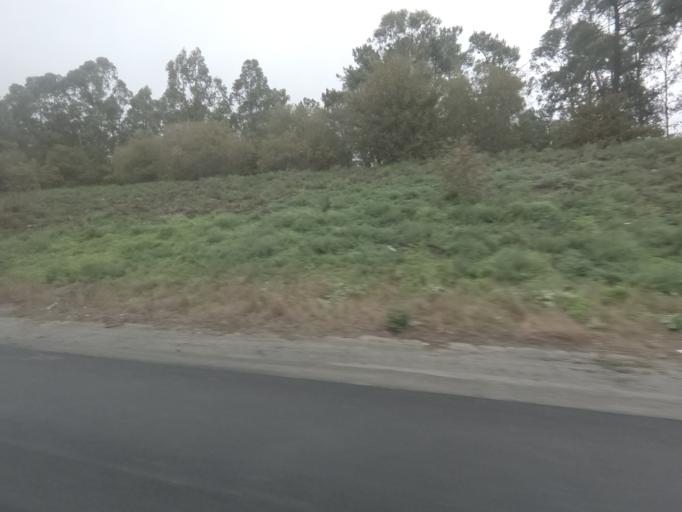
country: ES
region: Galicia
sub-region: Provincia de Pontevedra
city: Redondela
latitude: 42.2390
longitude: -8.6568
